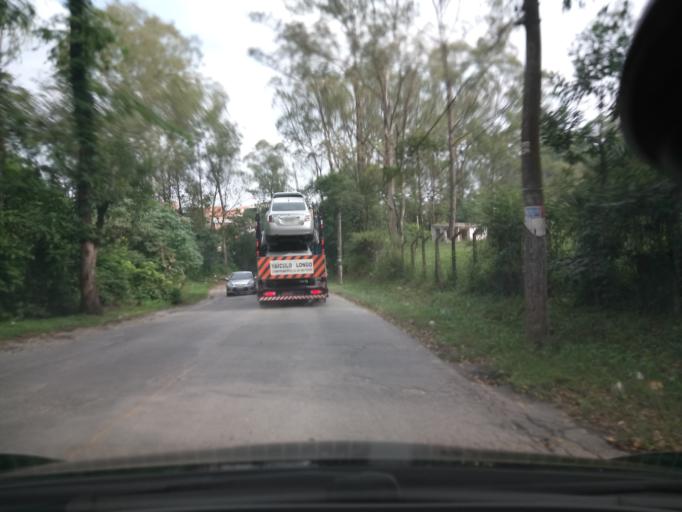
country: BR
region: Sao Paulo
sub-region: Sao Bernardo Do Campo
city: Sao Bernardo do Campo
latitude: -23.7497
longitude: -46.5929
